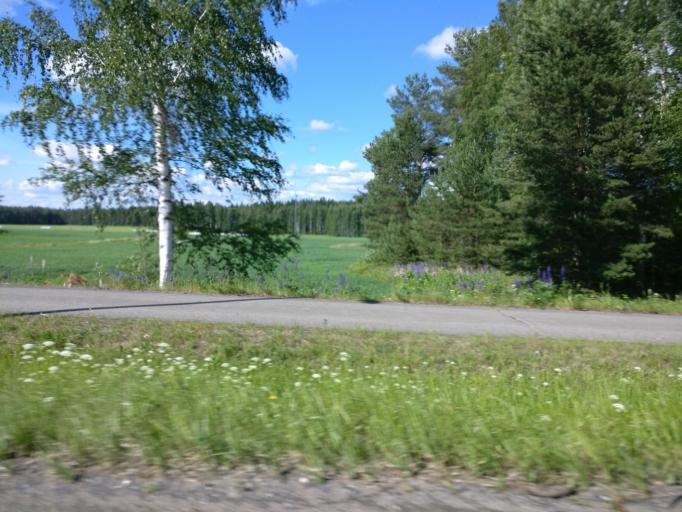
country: FI
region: Southern Savonia
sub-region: Savonlinna
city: Savonlinna
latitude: 61.8775
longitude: 28.9717
